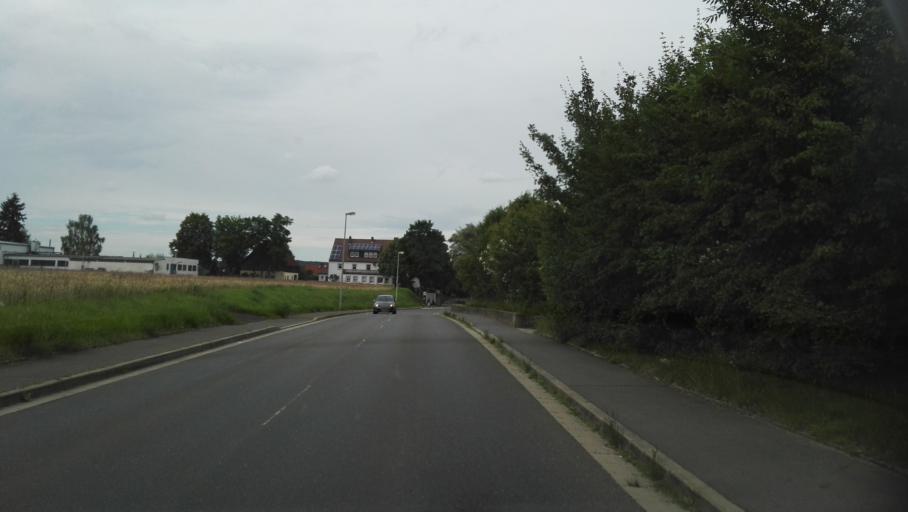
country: DE
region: Bavaria
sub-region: Upper Franconia
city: Plankenfels
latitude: 49.8861
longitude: 11.3345
